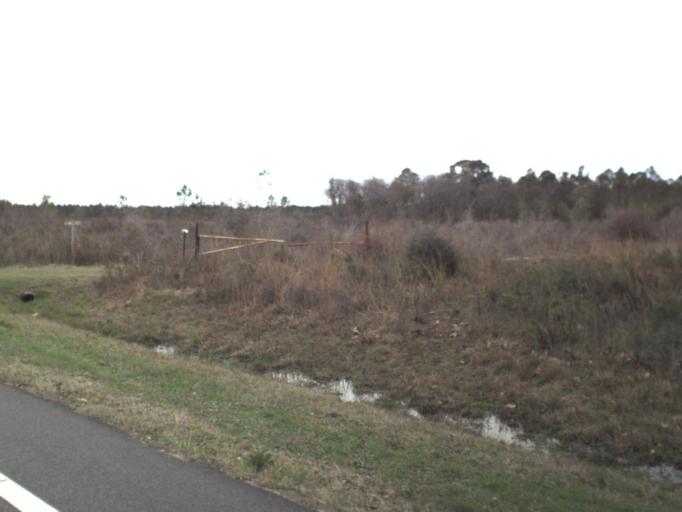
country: US
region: Florida
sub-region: Gulf County
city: Wewahitchka
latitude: 30.1413
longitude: -85.2722
